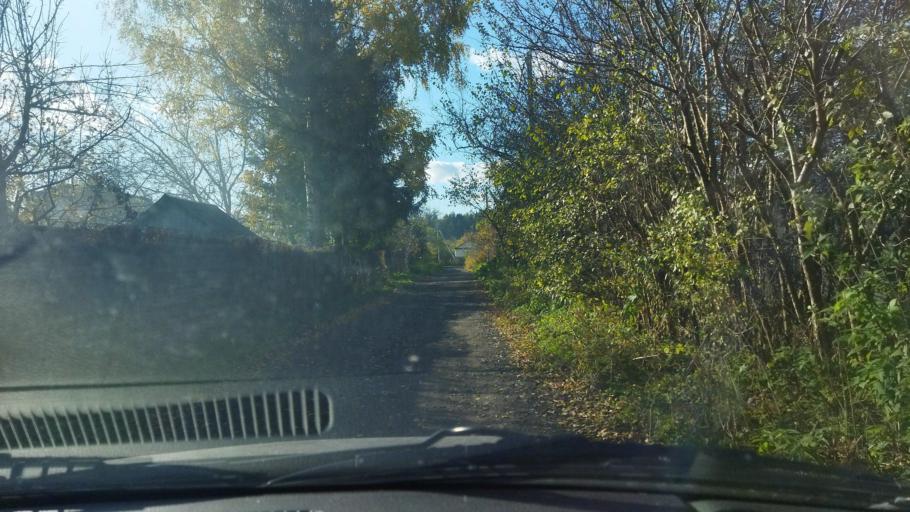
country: BY
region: Minsk
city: Slabada
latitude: 53.9884
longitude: 27.8953
